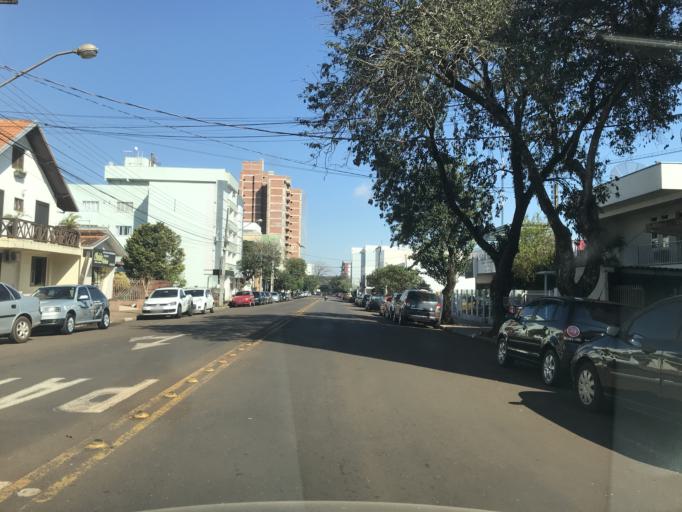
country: BR
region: Parana
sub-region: Toledo
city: Toledo
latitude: -24.7238
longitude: -53.7384
